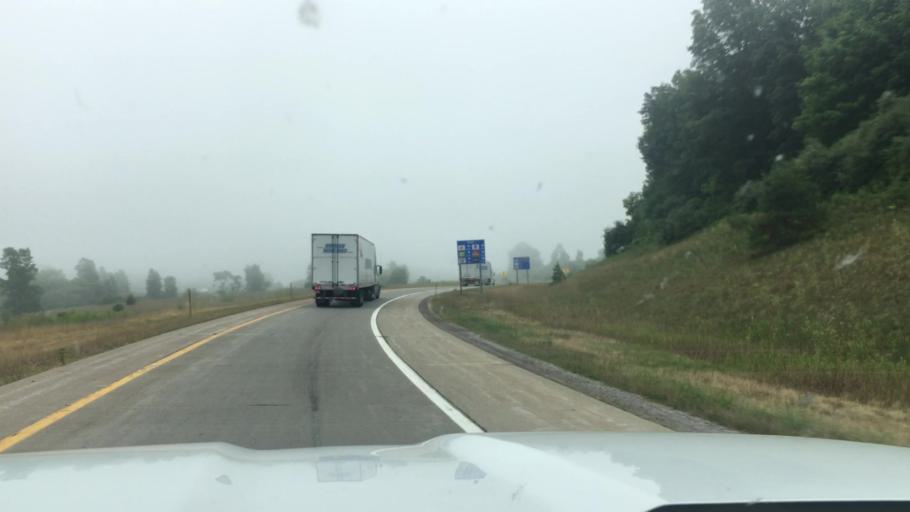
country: US
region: Michigan
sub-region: Shiawassee County
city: Perry
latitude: 42.8389
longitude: -84.2251
